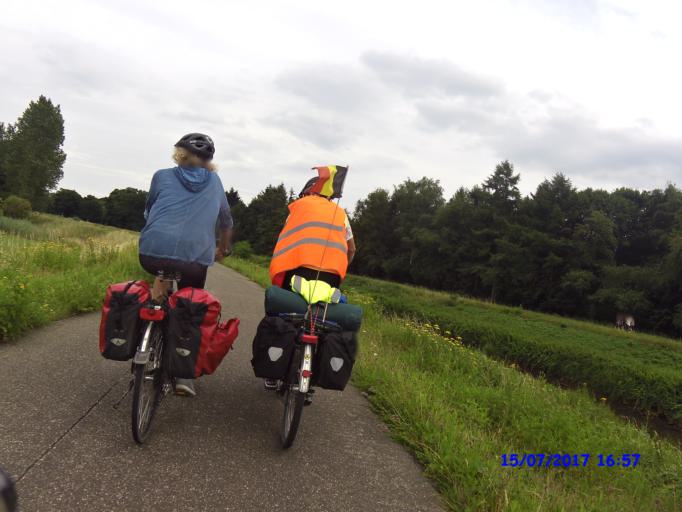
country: BE
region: Flanders
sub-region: Provincie Antwerpen
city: Grobbendonk
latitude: 51.1773
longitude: 4.7049
